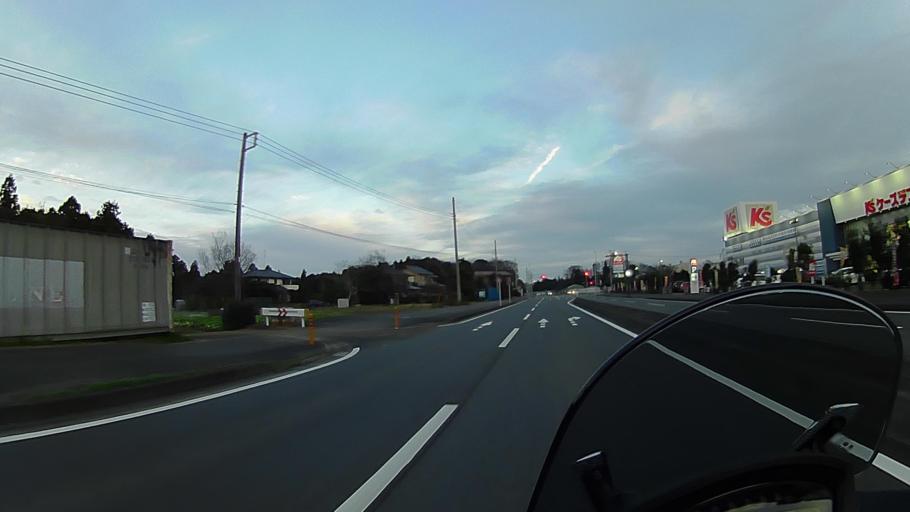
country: JP
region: Kanagawa
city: Atsugi
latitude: 35.4042
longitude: 139.4243
